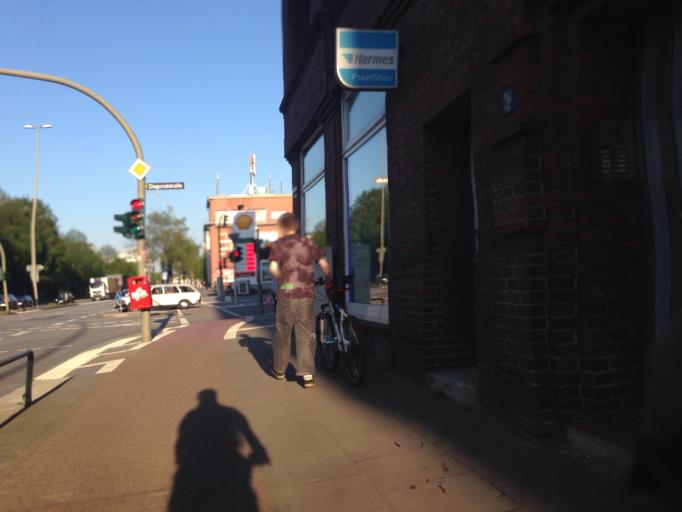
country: DE
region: Hamburg
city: Rothenburgsort
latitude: 53.5509
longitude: 10.0583
